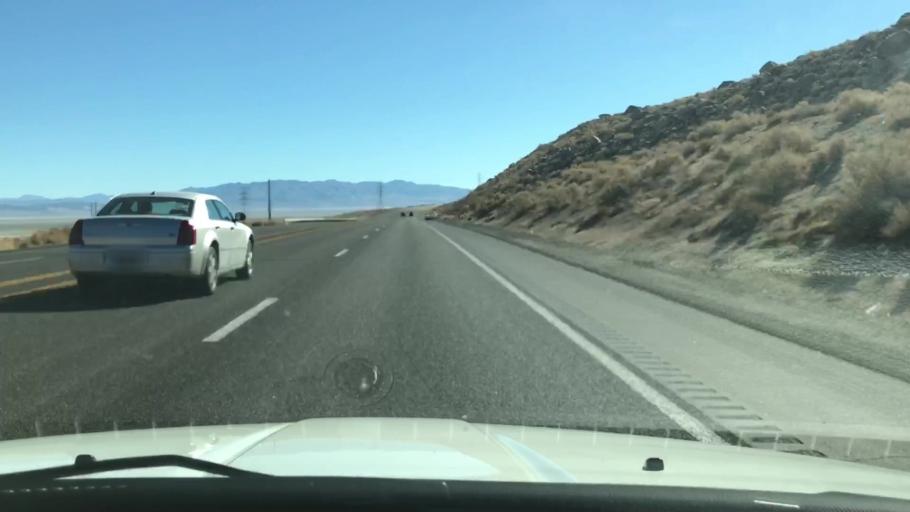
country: US
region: California
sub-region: Inyo County
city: Lone Pine
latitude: 36.5149
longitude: -118.0366
